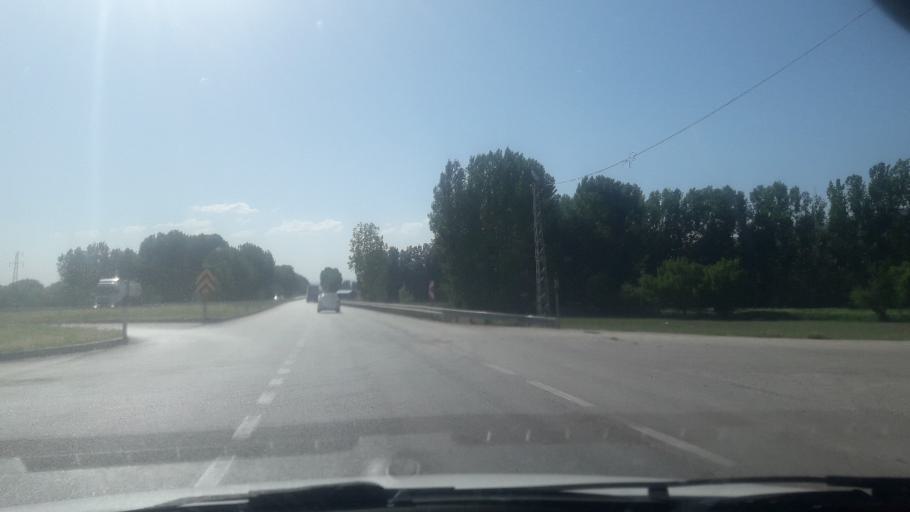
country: TR
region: Tokat
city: Yesilyurt
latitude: 40.3004
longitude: 36.3471
